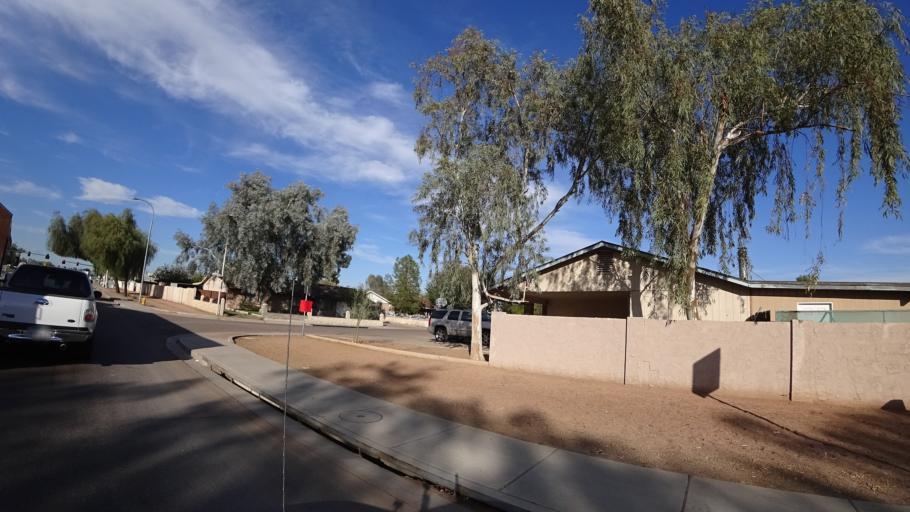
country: US
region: Arizona
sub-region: Maricopa County
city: Tolleson
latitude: 33.4573
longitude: -112.2034
